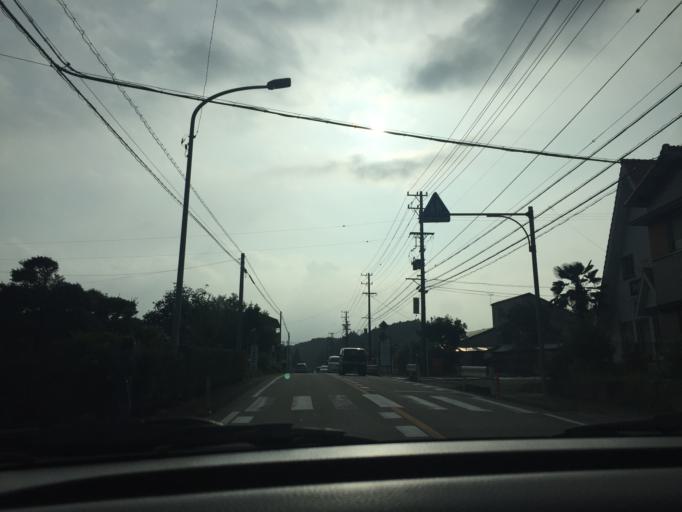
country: JP
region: Aichi
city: Shinshiro
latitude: 34.9307
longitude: 137.5696
